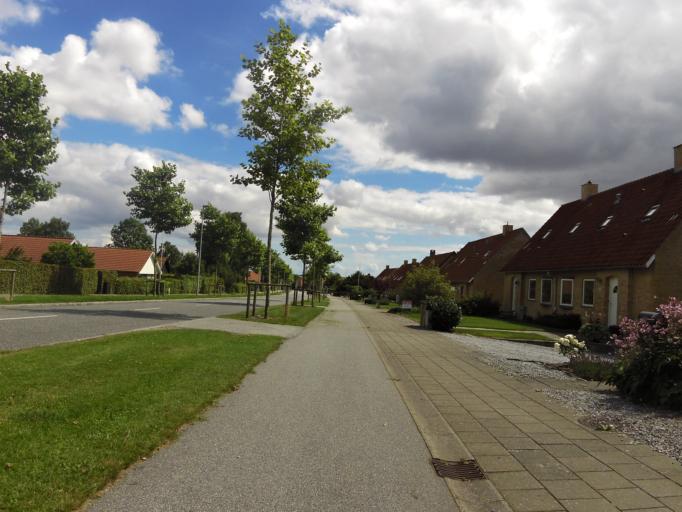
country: DK
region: South Denmark
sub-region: Haderslev Kommune
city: Haderslev
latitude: 55.2520
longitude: 9.4611
